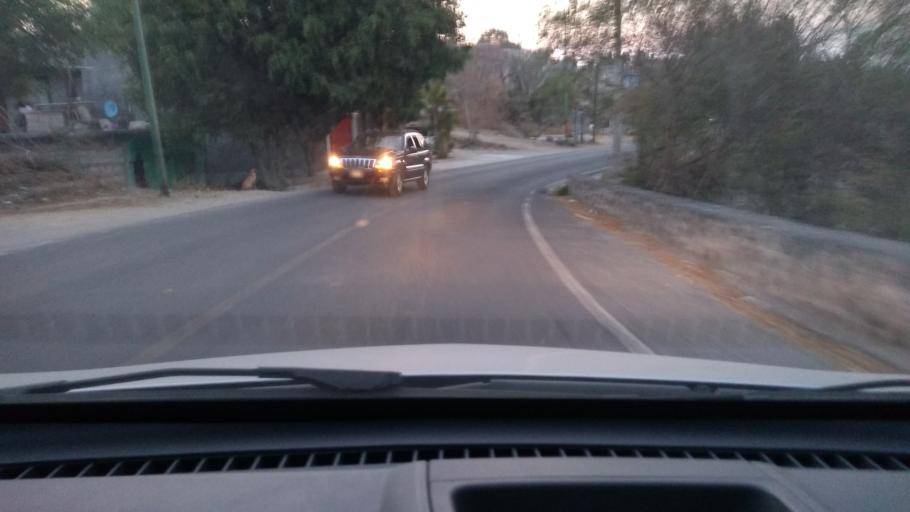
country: MX
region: Morelos
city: Coatetelco
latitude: 18.7233
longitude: -99.3157
